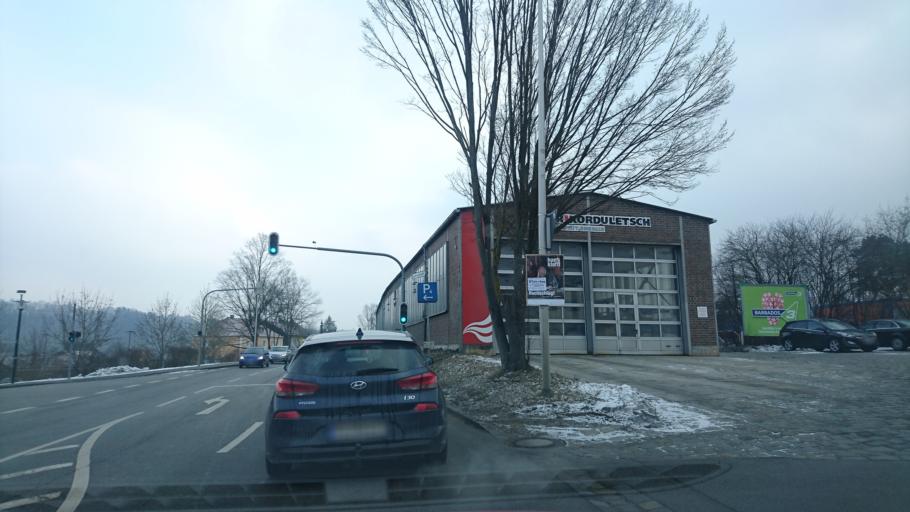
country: DE
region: Bavaria
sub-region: Lower Bavaria
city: Vilshofen
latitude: 48.6303
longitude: 13.1926
